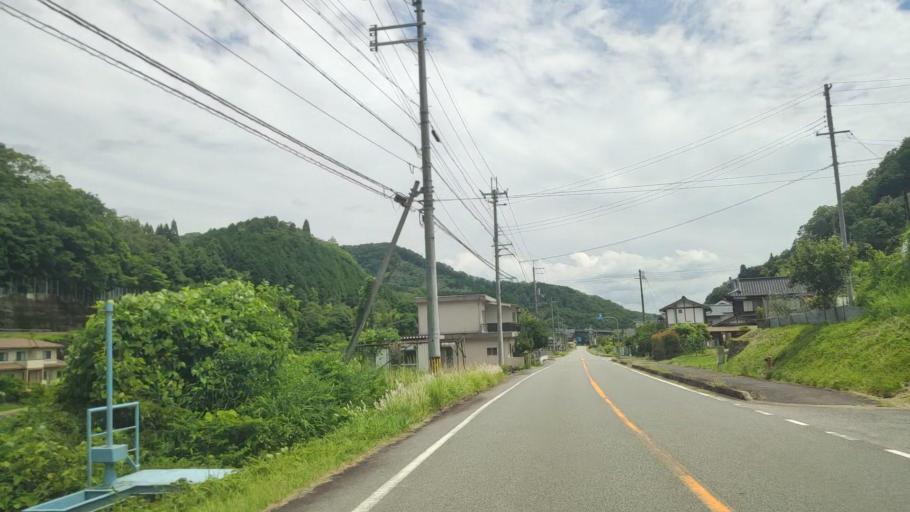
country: JP
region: Hyogo
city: Yamazakicho-nakabirose
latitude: 35.0632
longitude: 134.3639
